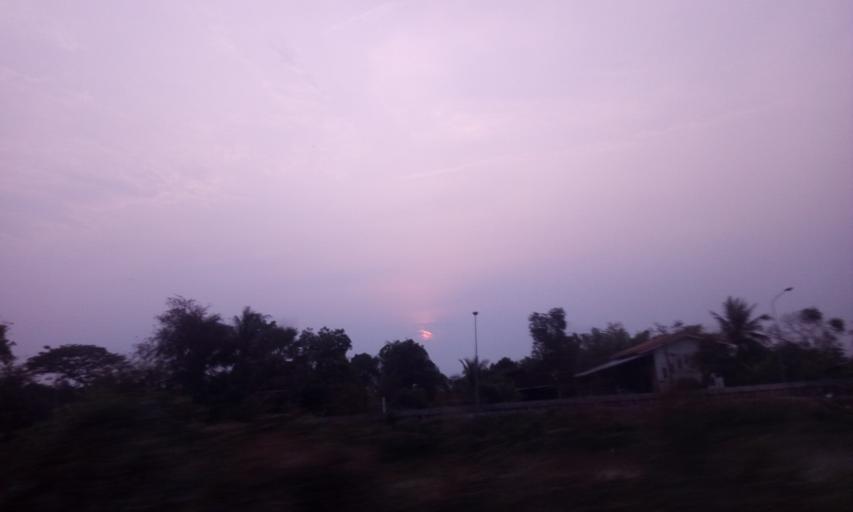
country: TH
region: Pathum Thani
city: Nong Suea
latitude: 14.0537
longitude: 100.8931
